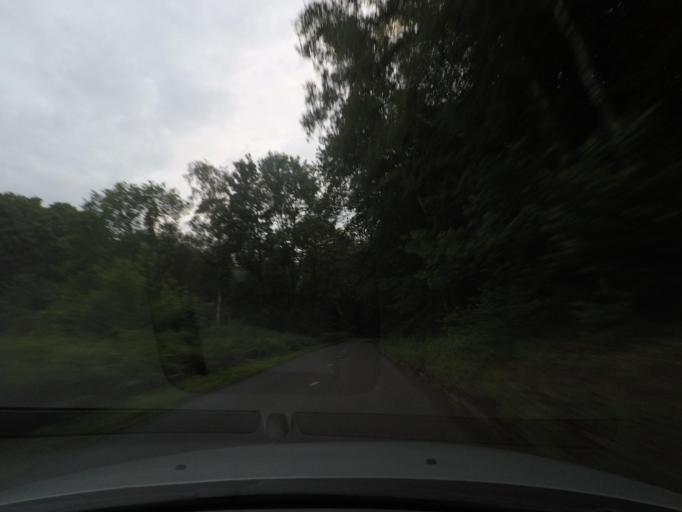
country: FR
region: Haute-Normandie
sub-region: Departement de la Seine-Maritime
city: Fontaine-le-Bourg
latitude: 49.5482
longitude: 1.1181
